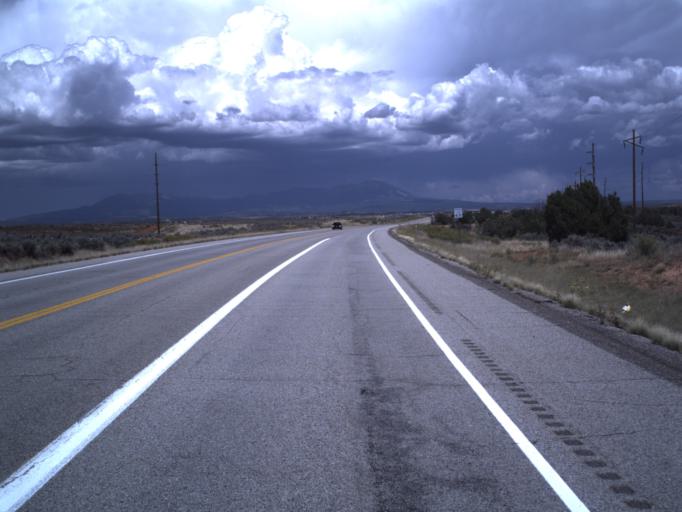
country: US
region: Utah
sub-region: San Juan County
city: Blanding
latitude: 37.5364
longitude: -109.4941
